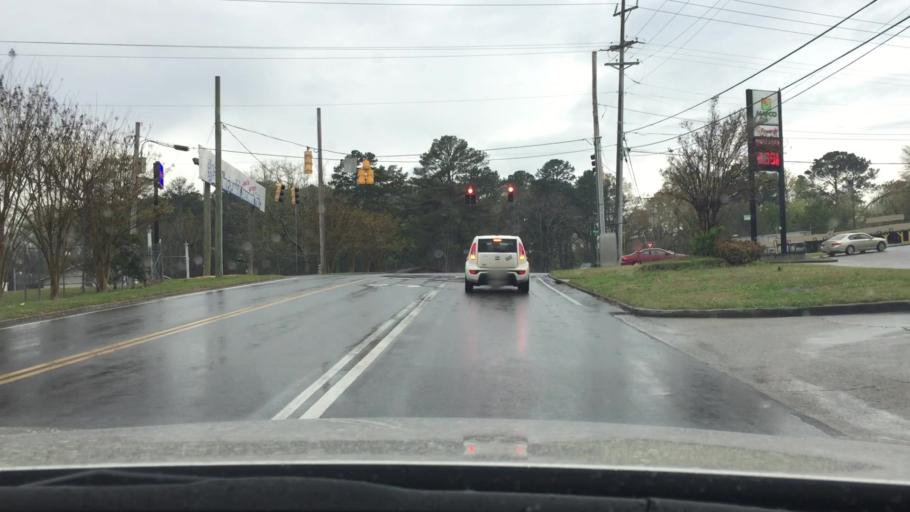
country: US
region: Georgia
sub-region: Catoosa County
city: Lakeview
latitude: 34.9776
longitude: -85.2440
